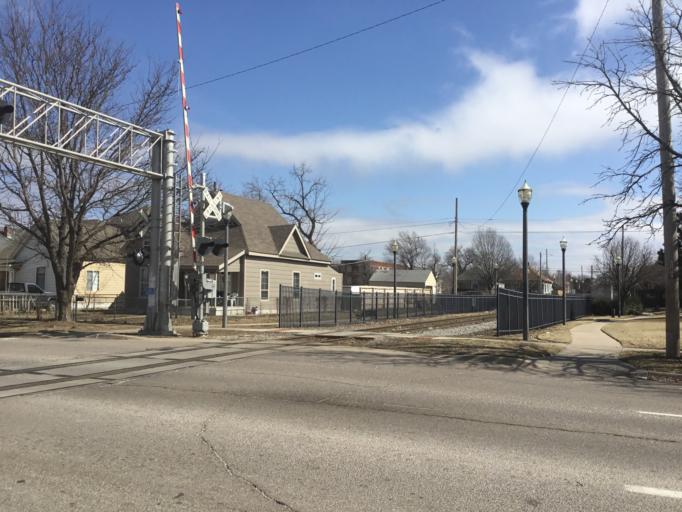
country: US
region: Kansas
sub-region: Sedgwick County
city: Wichita
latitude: 37.6697
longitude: -97.3382
